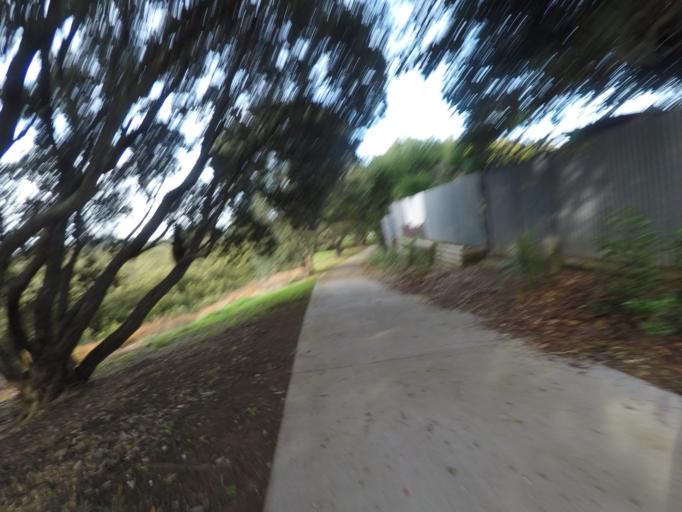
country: NZ
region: Auckland
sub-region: Auckland
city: Mangere
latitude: -36.9440
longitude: 174.7983
